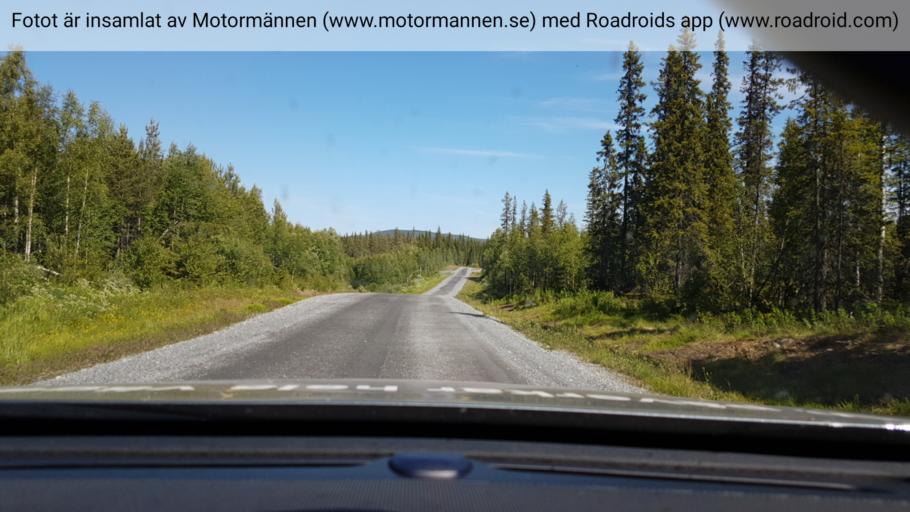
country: SE
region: Vaesterbotten
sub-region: Vilhelmina Kommun
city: Sjoberg
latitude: 64.7974
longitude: 15.9923
